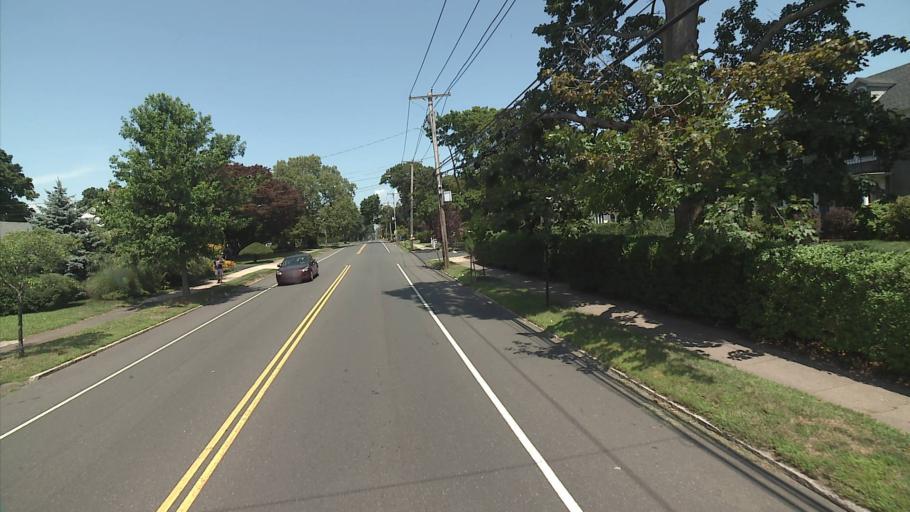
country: US
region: Connecticut
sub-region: New Haven County
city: East Haven
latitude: 41.2731
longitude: -72.8967
